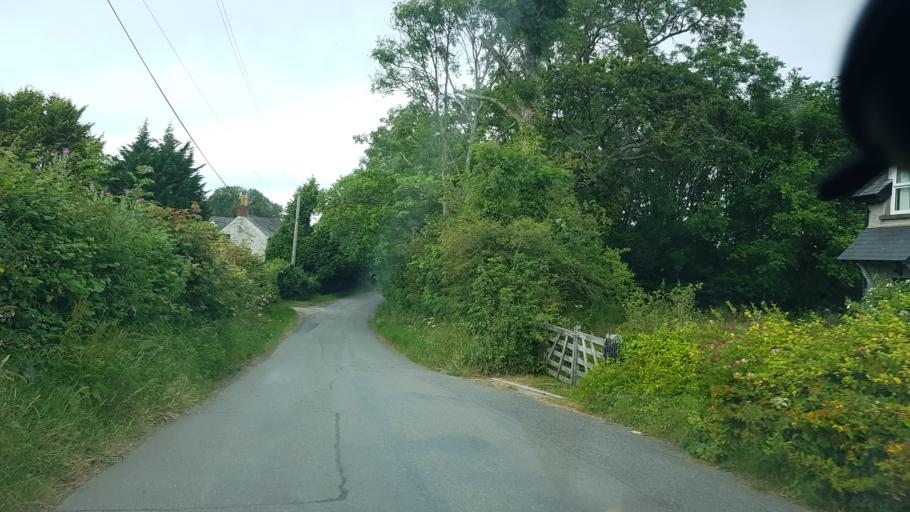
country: GB
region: Wales
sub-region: Pembrokeshire
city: Wiston
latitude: 51.7914
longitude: -4.8906
